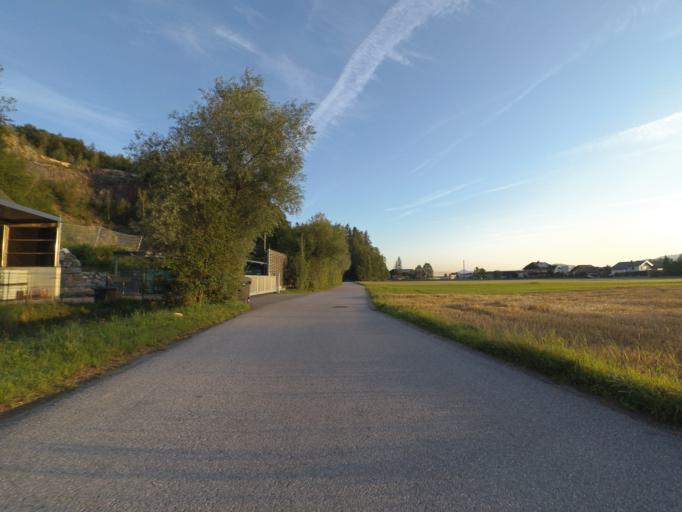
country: AT
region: Salzburg
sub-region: Politischer Bezirk Salzburg-Umgebung
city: Grodig
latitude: 47.7412
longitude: 13.0310
